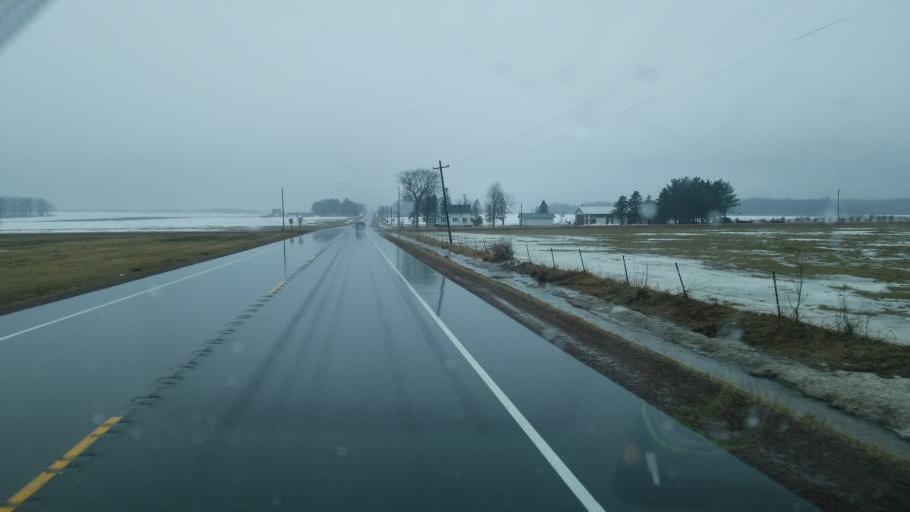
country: US
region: Wisconsin
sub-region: Marathon County
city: Spencer
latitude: 44.6561
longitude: -90.3143
